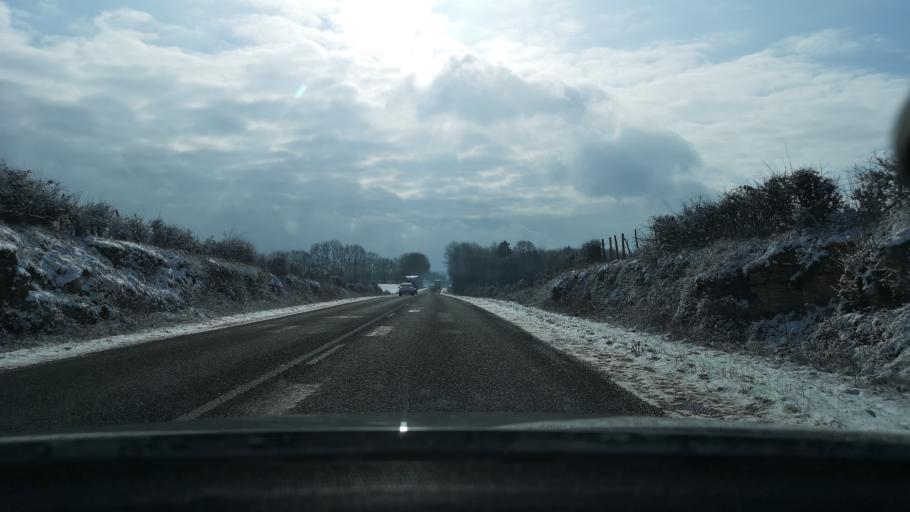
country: FR
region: Franche-Comte
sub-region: Departement du Jura
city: Orgelet
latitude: 46.5656
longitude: 5.5948
